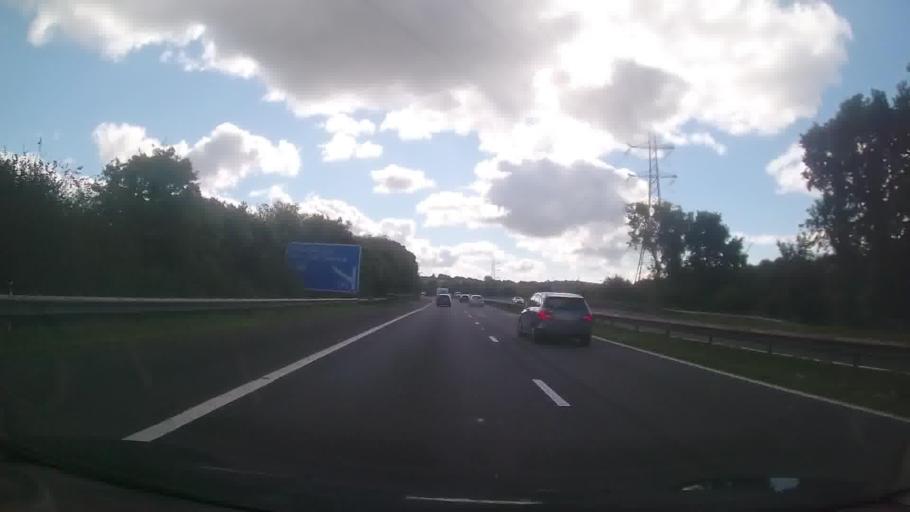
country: GB
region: Wales
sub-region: City and County of Swansea
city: Clydach
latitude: 51.6710
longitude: -3.8913
